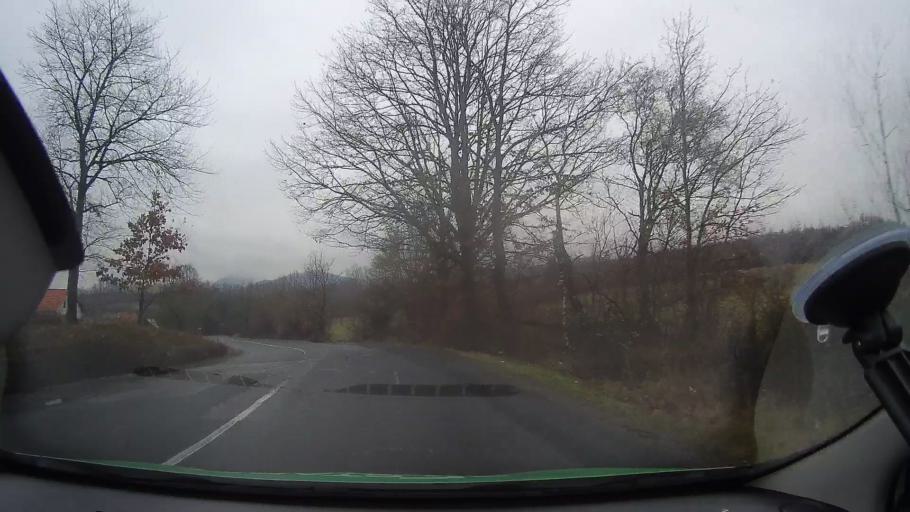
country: RO
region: Arad
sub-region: Comuna Varfurile
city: Varfurile
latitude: 46.3229
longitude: 22.4961
